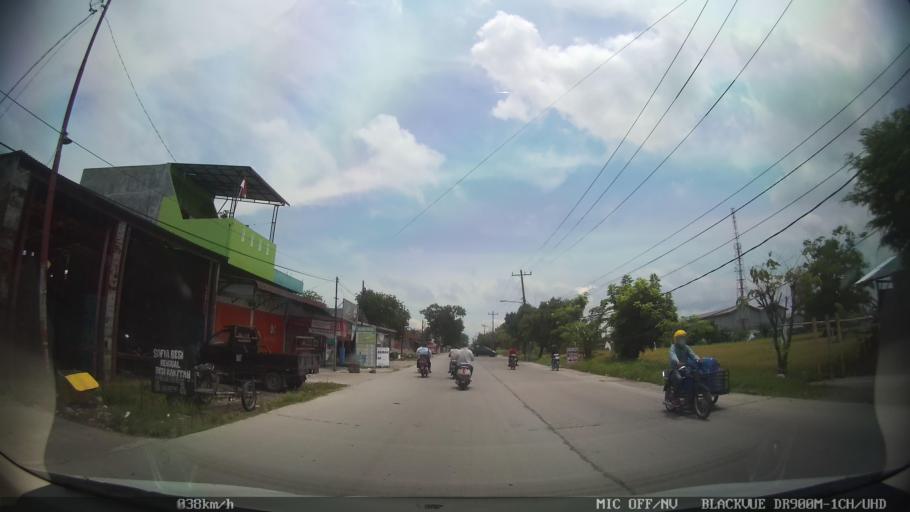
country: ID
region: North Sumatra
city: Labuhan Deli
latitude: 3.6897
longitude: 98.6848
